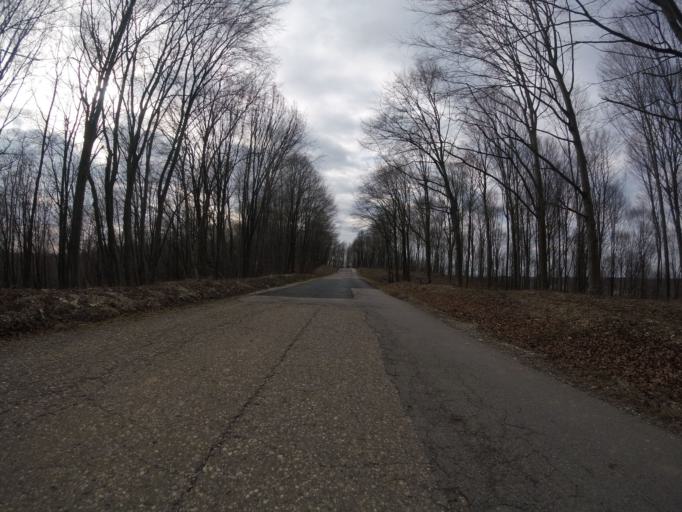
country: HR
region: Zagrebacka
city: Mraclin
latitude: 45.5240
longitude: 16.0486
